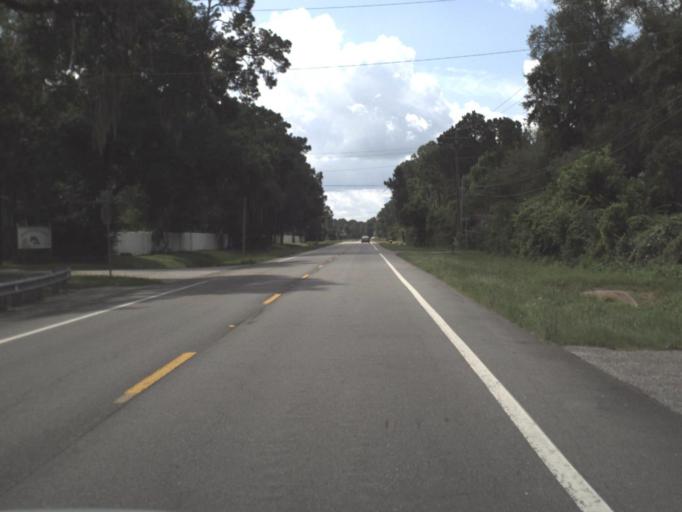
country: US
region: Florida
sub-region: Clay County
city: Green Cove Springs
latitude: 30.0016
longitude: -81.6039
